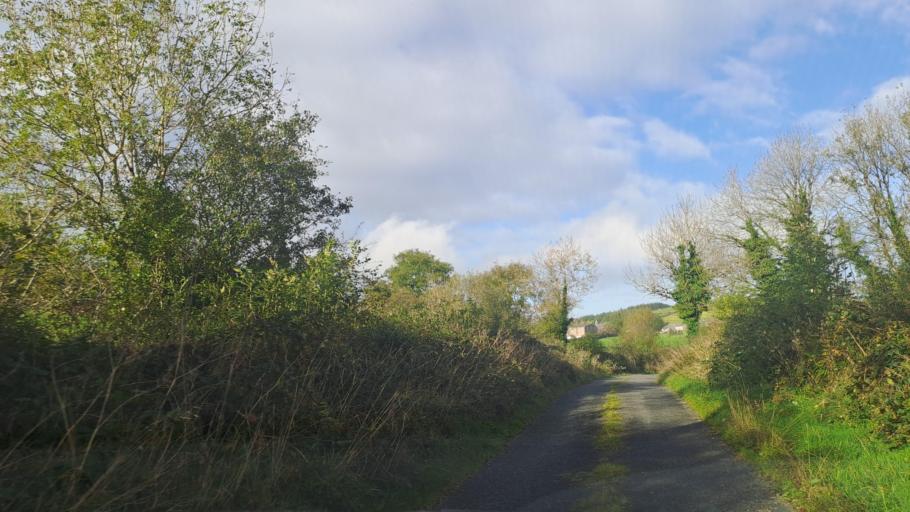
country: IE
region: Ulster
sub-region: An Cabhan
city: Kingscourt
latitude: 54.0059
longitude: -6.8201
